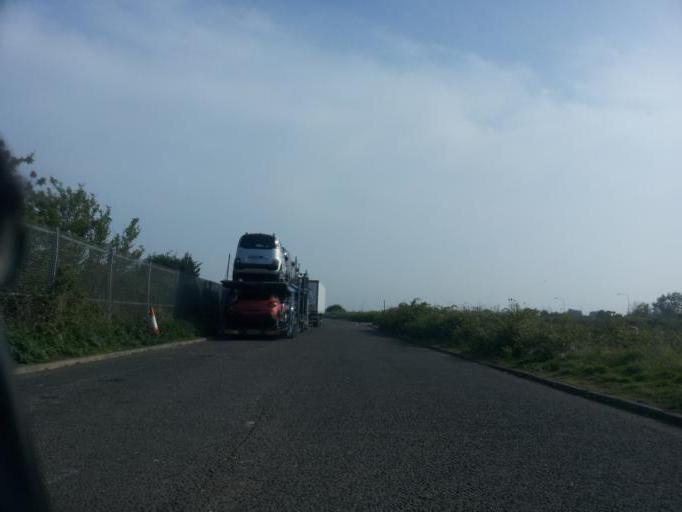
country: GB
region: England
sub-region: Kent
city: Queenborough
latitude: 51.4279
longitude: 0.7449
